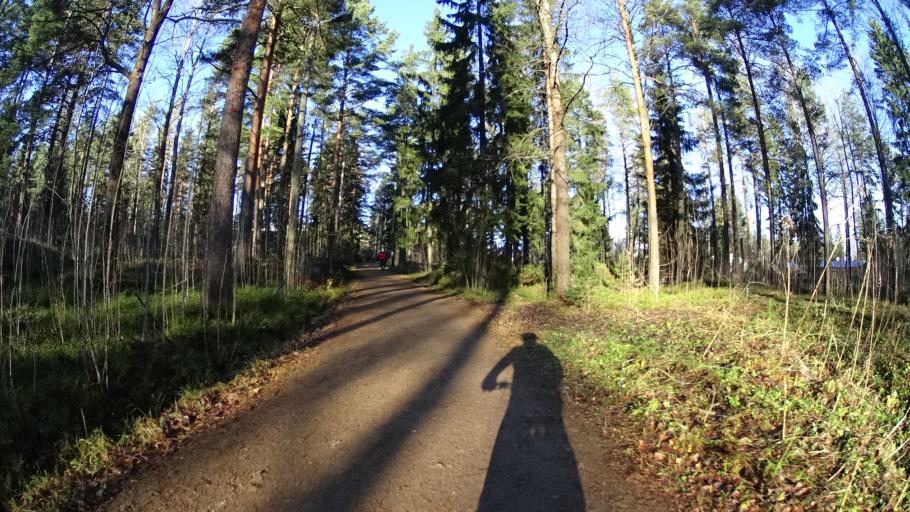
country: FI
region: Uusimaa
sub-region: Helsinki
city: Helsinki
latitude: 60.2304
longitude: 24.9129
